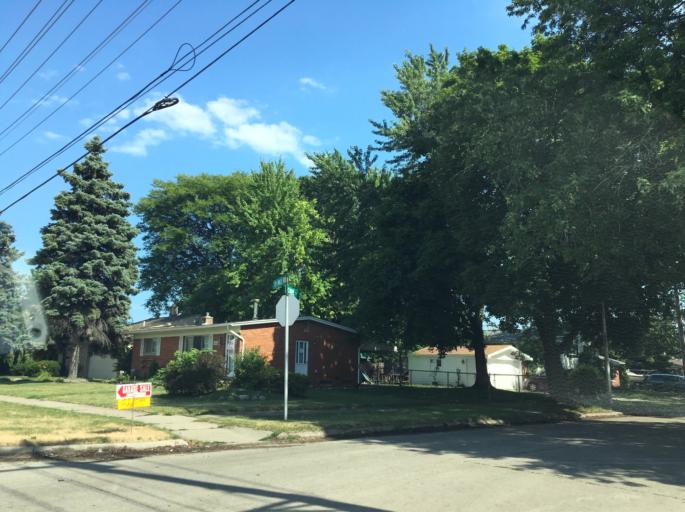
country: US
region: Michigan
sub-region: Macomb County
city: Fraser
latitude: 42.5542
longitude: -82.9214
